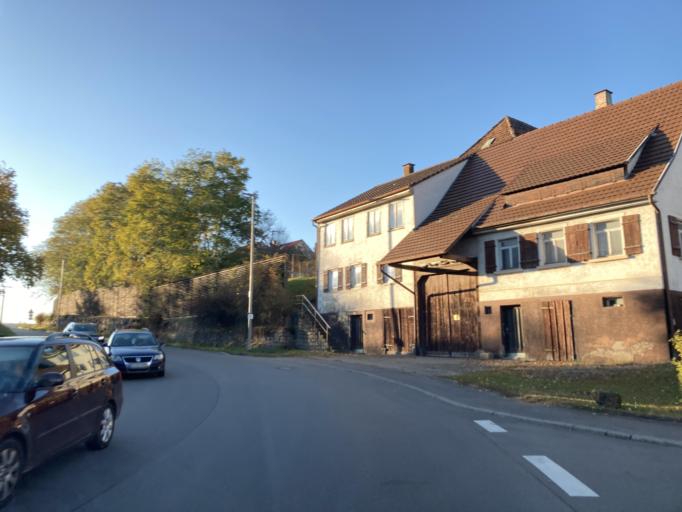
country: DE
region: Baden-Wuerttemberg
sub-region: Tuebingen Region
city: Rottenburg
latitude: 48.4383
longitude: 8.9341
